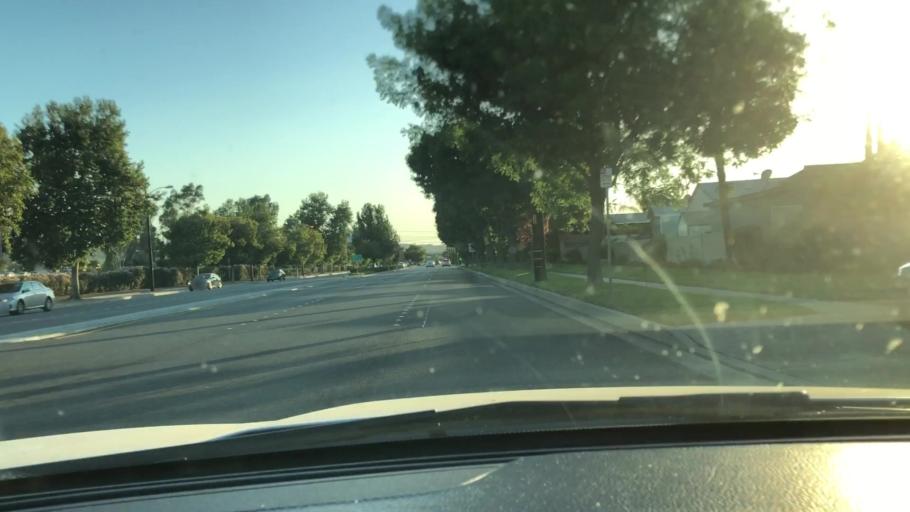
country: US
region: California
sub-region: Los Angeles County
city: Santa Clarita
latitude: 34.4217
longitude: -118.4919
